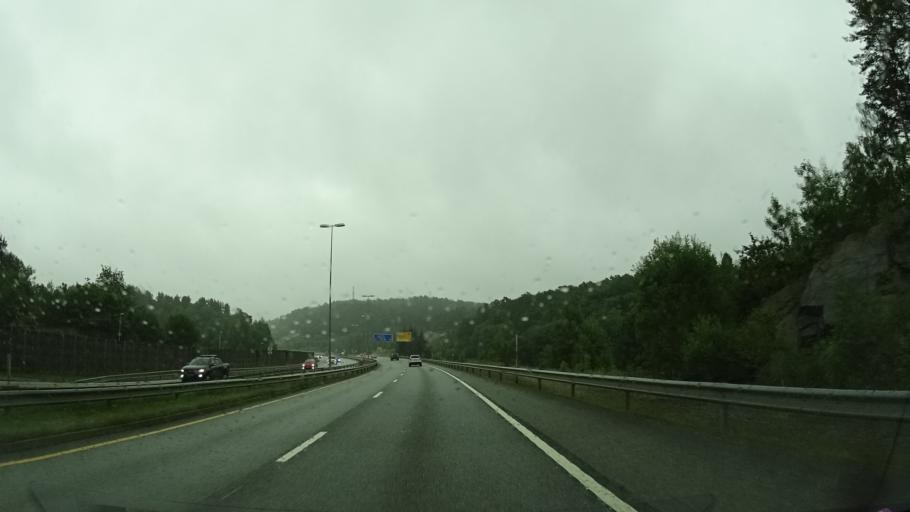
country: NO
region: Vest-Agder
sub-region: Kristiansand
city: Tveit
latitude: 58.1676
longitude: 8.1025
